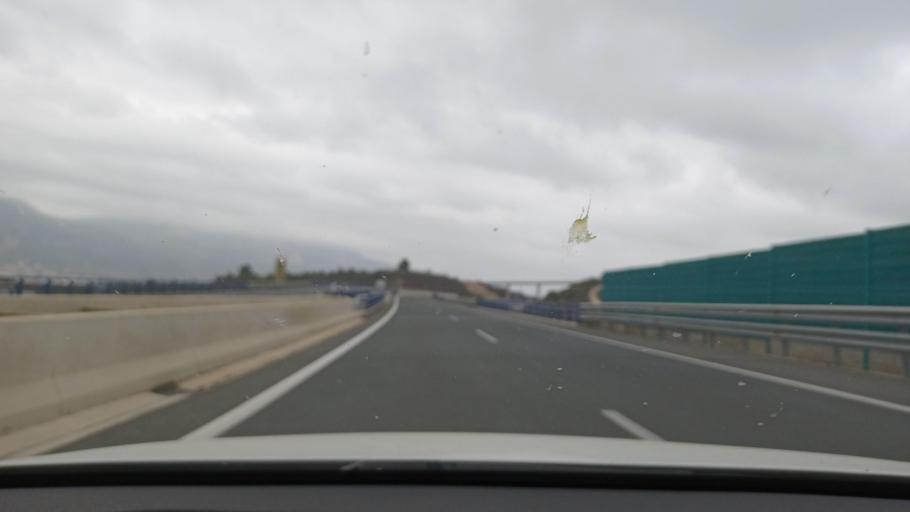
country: ES
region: Valencia
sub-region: Provincia de Alicante
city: Alcoy
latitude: 38.6822
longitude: -0.4610
